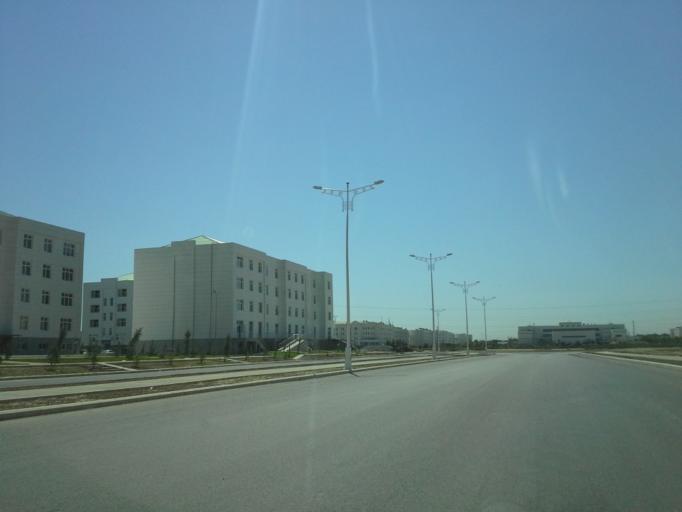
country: TM
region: Ahal
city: Ashgabat
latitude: 37.9717
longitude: 58.3263
